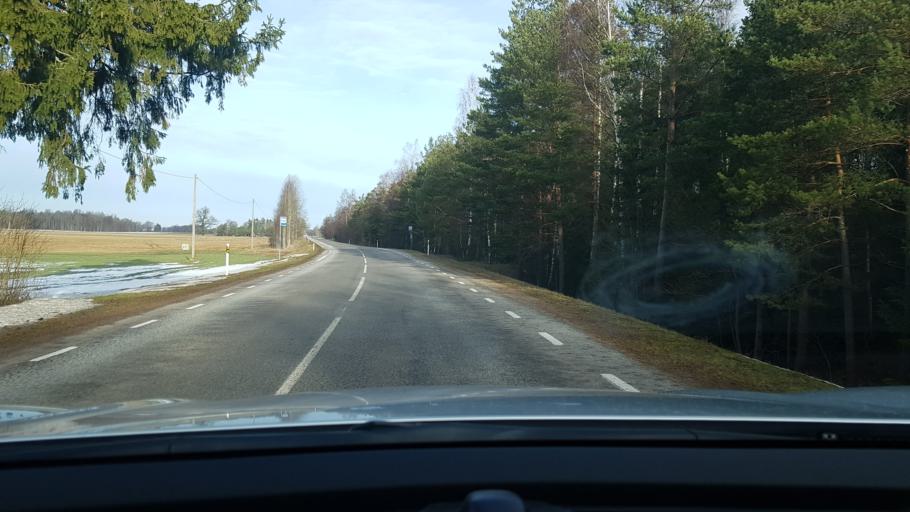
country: EE
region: Saare
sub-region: Kuressaare linn
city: Kuressaare
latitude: 58.4906
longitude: 22.7094
